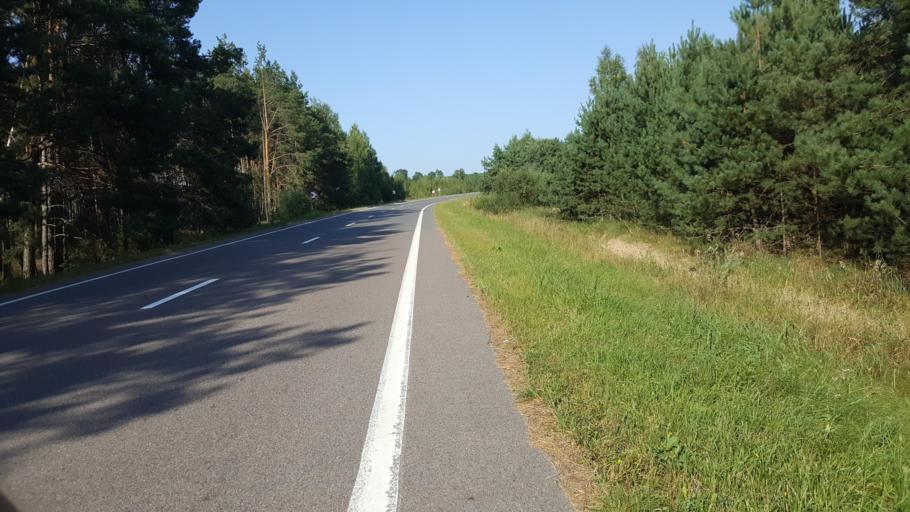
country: PL
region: Podlasie
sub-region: Powiat hajnowski
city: Hajnowka
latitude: 52.5616
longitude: 23.6060
